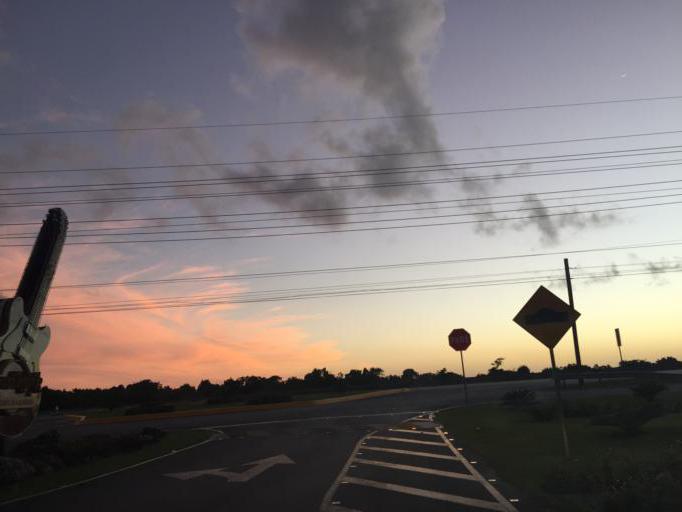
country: DO
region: San Juan
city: Punta Cana
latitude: 18.7210
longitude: -68.4855
